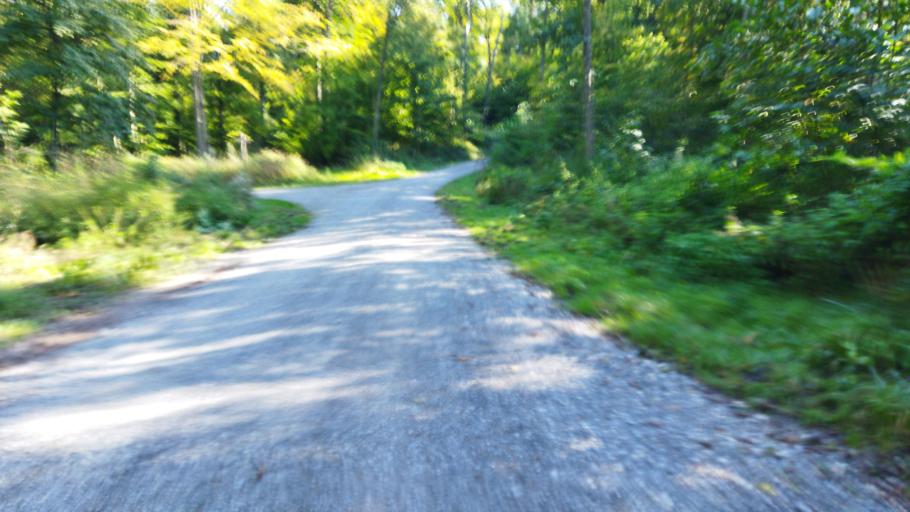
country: DE
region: Baden-Wuerttemberg
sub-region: Regierungsbezirk Stuttgart
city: Ilsfeld
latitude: 49.0340
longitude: 9.2563
